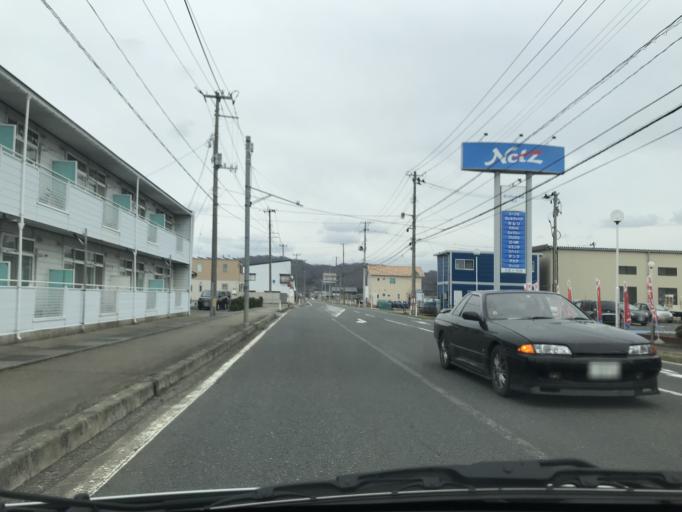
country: JP
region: Iwate
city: Kitakami
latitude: 39.2725
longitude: 141.1060
